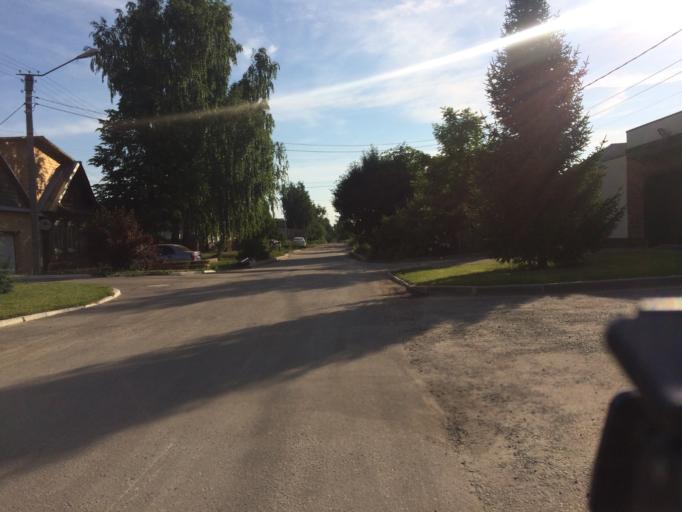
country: RU
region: Mariy-El
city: Yoshkar-Ola
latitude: 56.6470
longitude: 47.9124
